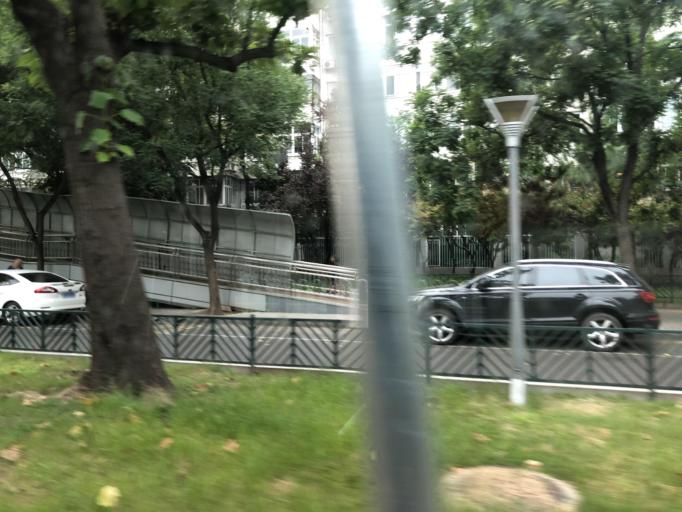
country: CN
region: Beijing
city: Sijiqing
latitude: 39.9312
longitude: 116.3100
